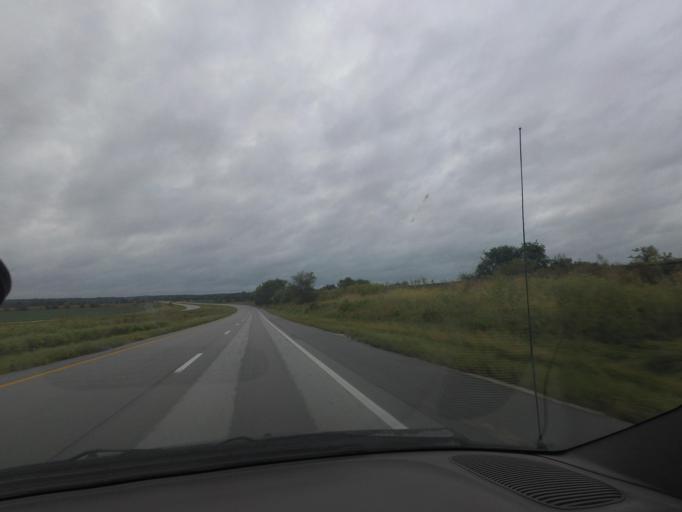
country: US
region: Missouri
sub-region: Shelby County
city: Shelbina
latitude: 39.6673
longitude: -91.9277
